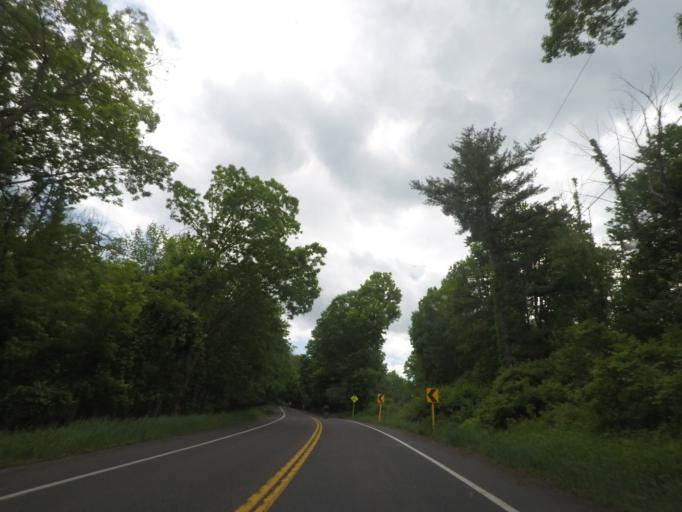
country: US
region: New York
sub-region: Dutchess County
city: Pine Plains
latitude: 42.0816
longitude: -73.6729
